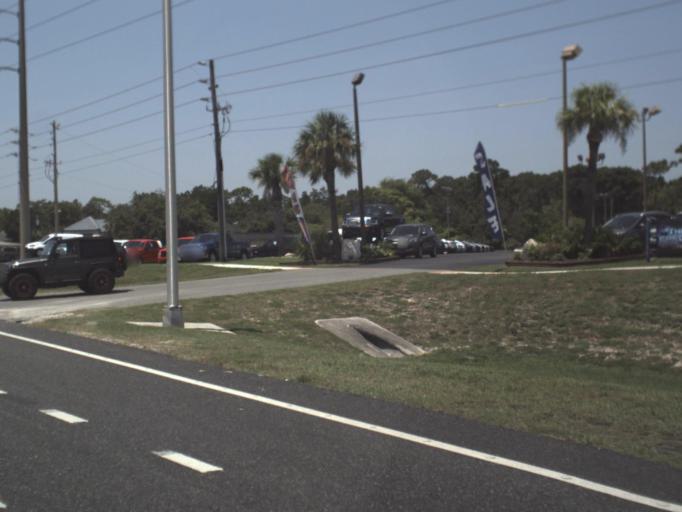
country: US
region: Florida
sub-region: Hernando County
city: Timber Pines
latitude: 28.4798
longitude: -82.6100
